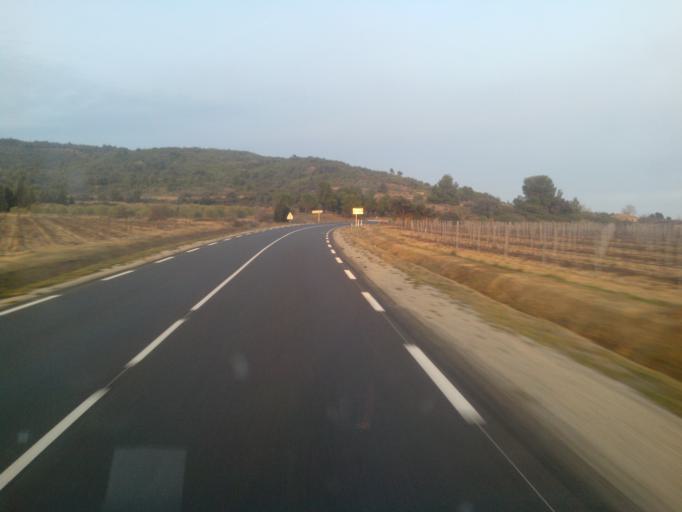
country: FR
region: Languedoc-Roussillon
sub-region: Departement de l'Herault
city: Olonzac
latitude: 43.2738
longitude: 2.7697
